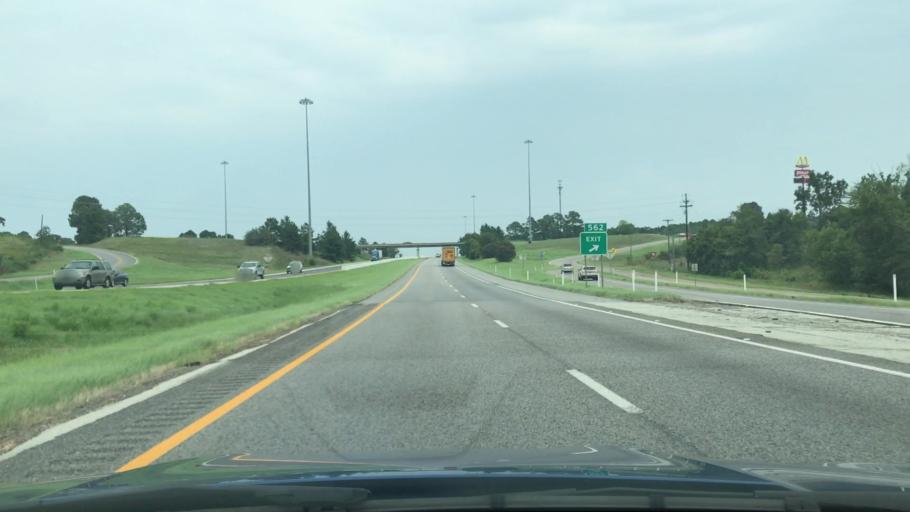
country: US
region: Texas
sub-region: Smith County
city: Tyler
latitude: 32.4537
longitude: -95.2878
